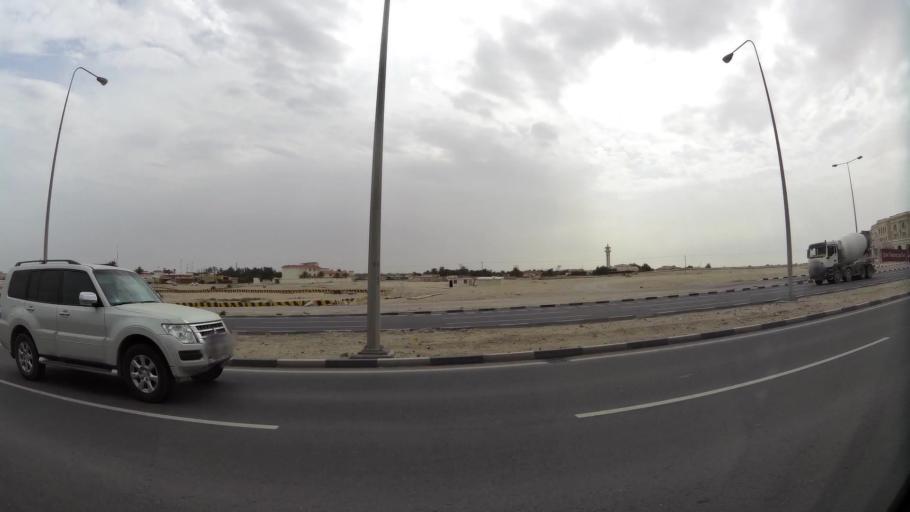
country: QA
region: Baladiyat ad Dawhah
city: Doha
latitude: 25.3311
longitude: 51.5014
